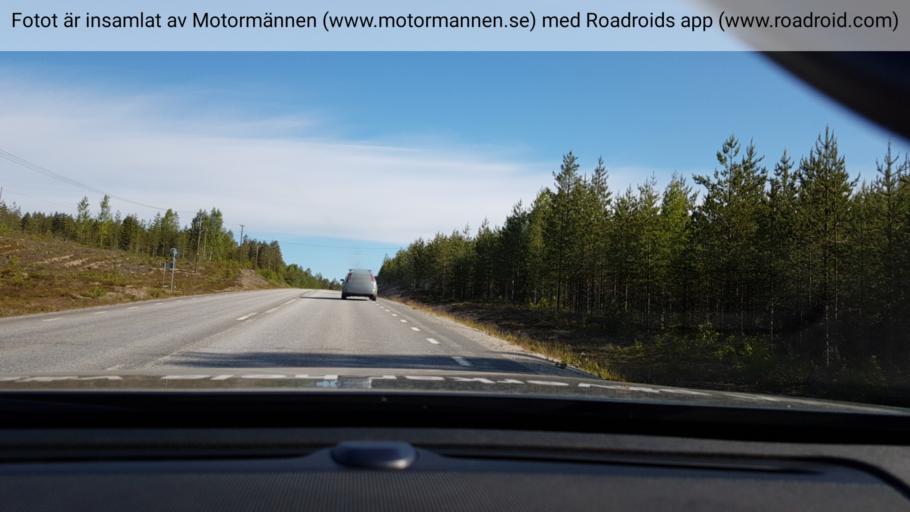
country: SE
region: Vaesterbotten
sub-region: Vannas Kommun
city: Vaennaes
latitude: 64.0284
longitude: 19.6926
